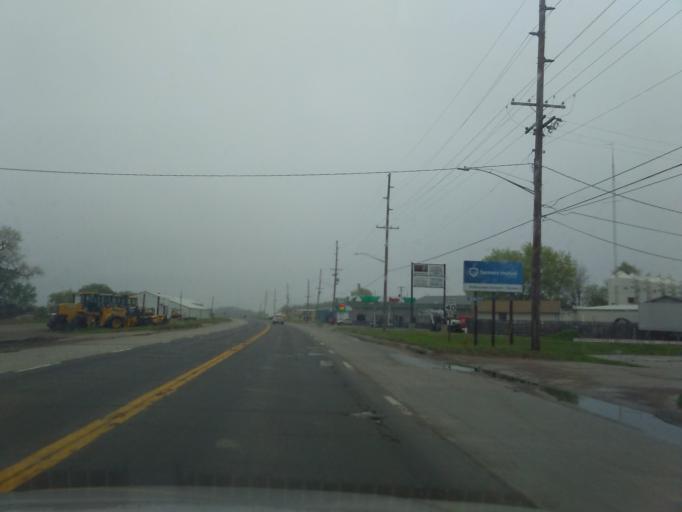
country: US
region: Nebraska
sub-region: Cuming County
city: Wisner
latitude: 41.9288
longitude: -96.8124
